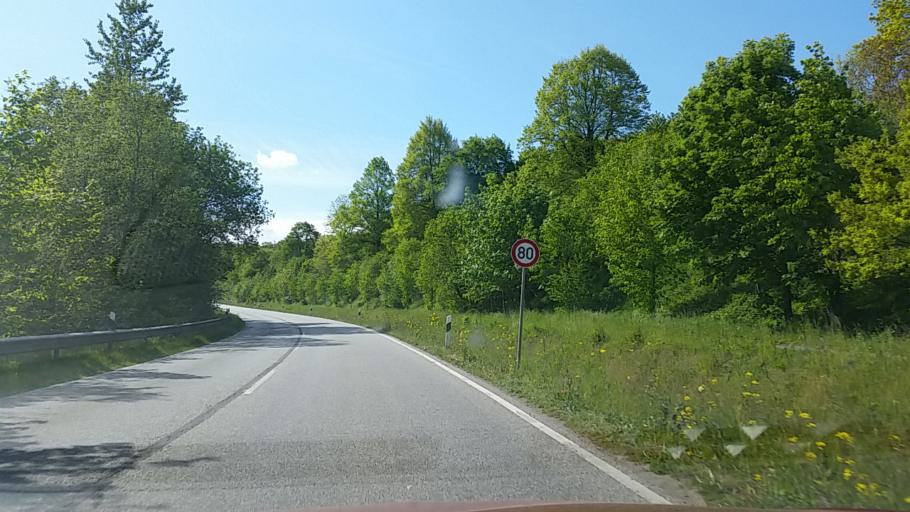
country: DE
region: Schleswig-Holstein
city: Meddewade
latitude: 53.8153
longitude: 10.4141
